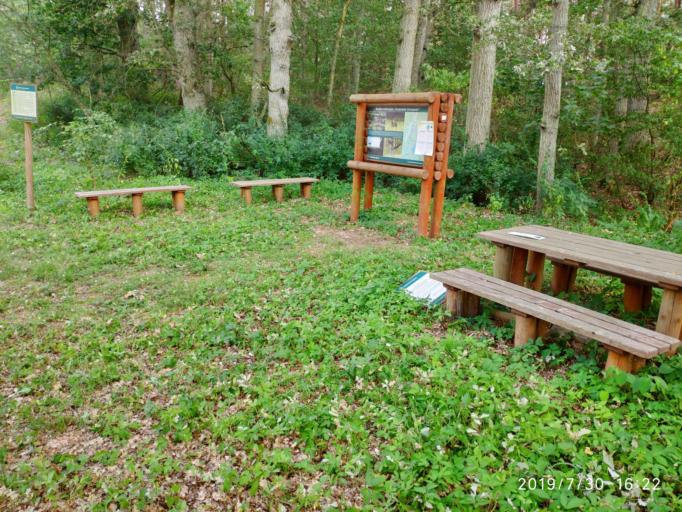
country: PL
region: Lubusz
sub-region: Powiat krosnienski
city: Bytnica
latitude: 52.1844
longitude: 15.2749
